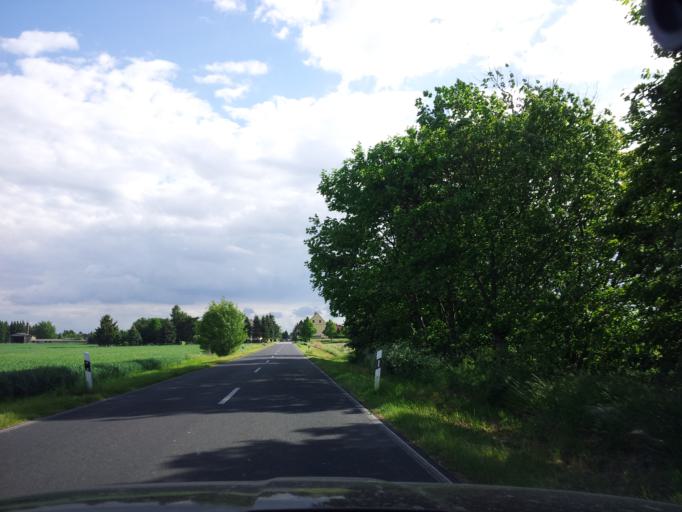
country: DE
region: Saxony-Anhalt
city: Seyda
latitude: 51.9602
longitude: 12.8978
